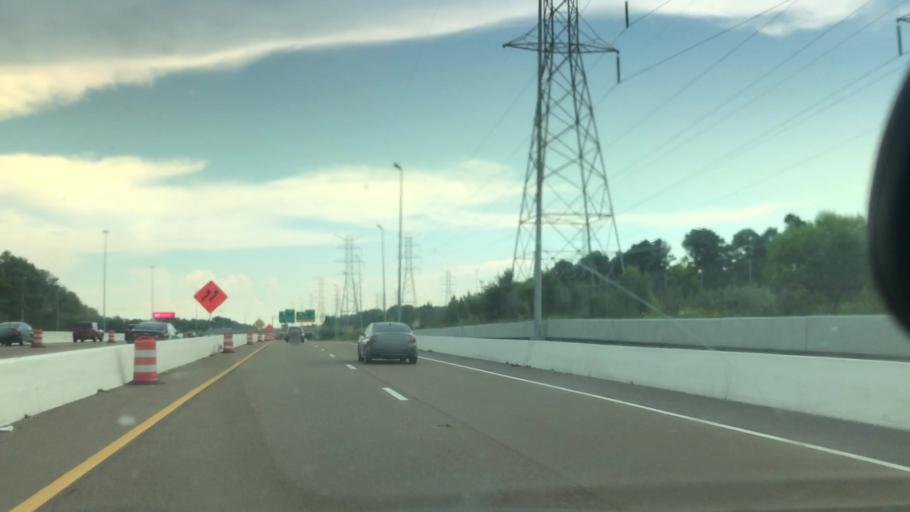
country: US
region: Tennessee
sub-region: Shelby County
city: Germantown
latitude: 35.1061
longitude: -89.8703
